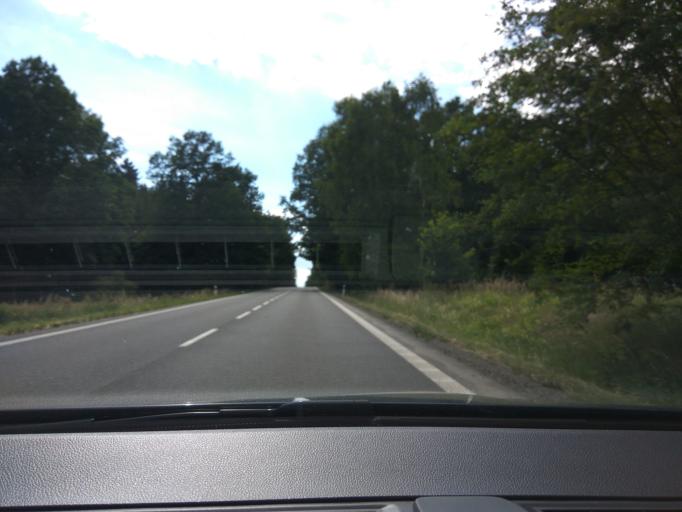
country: CZ
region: Jihocesky
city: Cimelice
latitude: 49.5013
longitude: 14.1487
